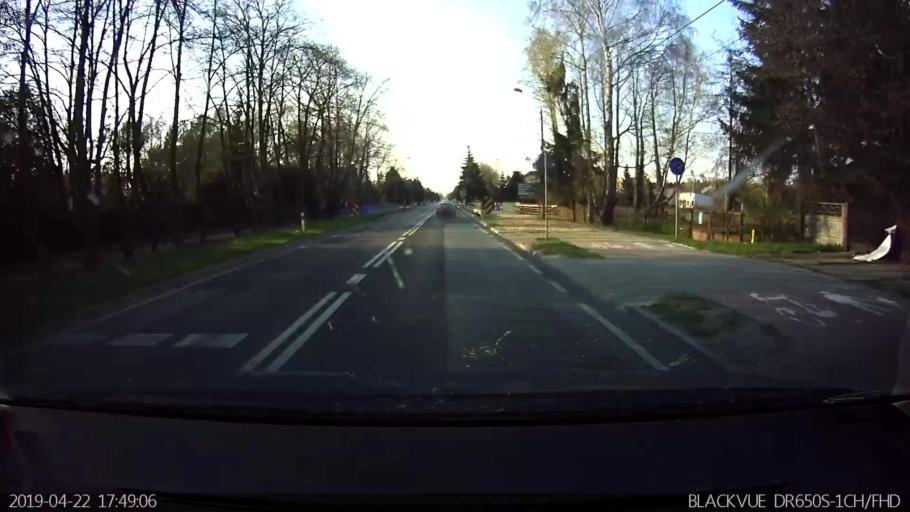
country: PL
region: Masovian Voivodeship
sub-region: Powiat wegrowski
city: Wegrow
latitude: 52.4109
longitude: 22.0108
